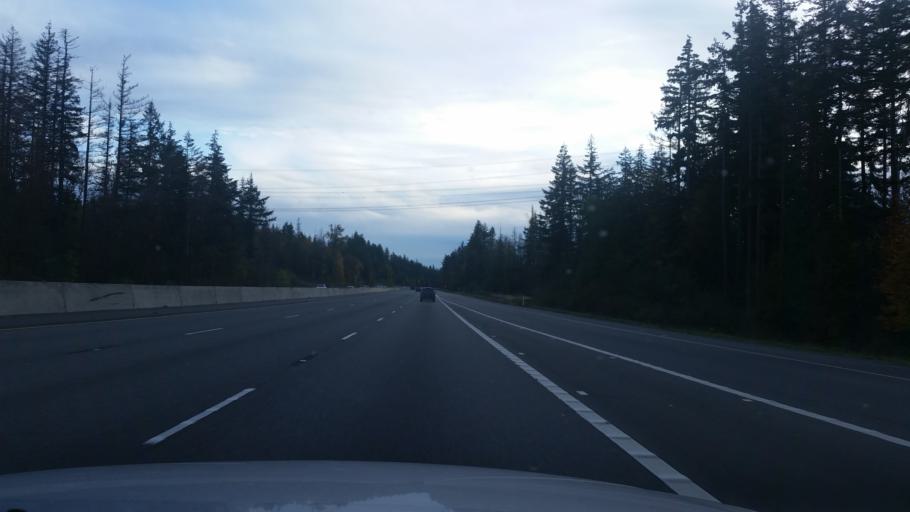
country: US
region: Washington
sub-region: Thurston County
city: Grand Mound
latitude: 46.8686
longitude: -122.9700
